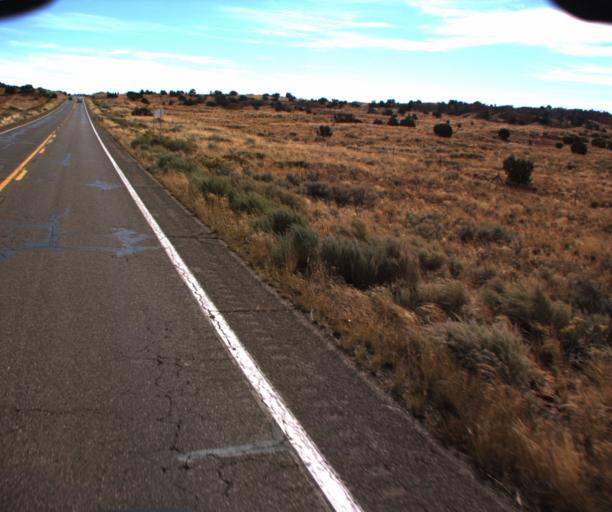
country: US
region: Arizona
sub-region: Coconino County
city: Kaibito
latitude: 36.5806
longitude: -111.1414
